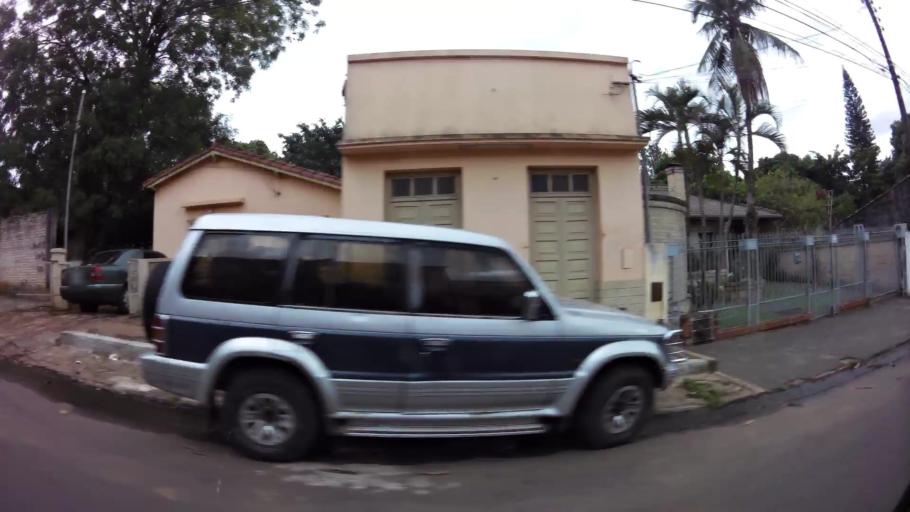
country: PY
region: Central
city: San Lorenzo
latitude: -25.2673
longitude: -57.4966
